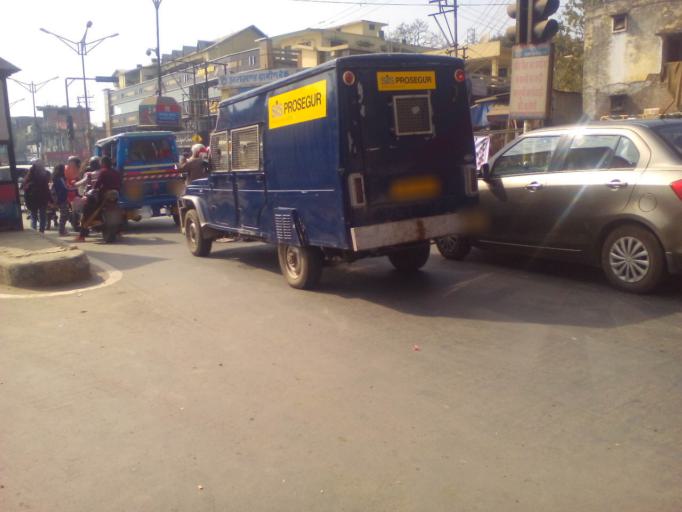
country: IN
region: Uttarakhand
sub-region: Dehradun
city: Dehradun
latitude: 30.3211
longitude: 78.0414
